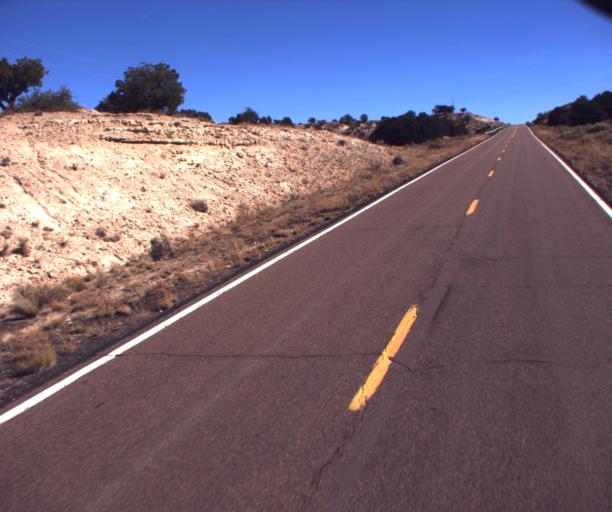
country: US
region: Arizona
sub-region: Navajo County
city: First Mesa
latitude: 35.7606
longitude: -109.9682
